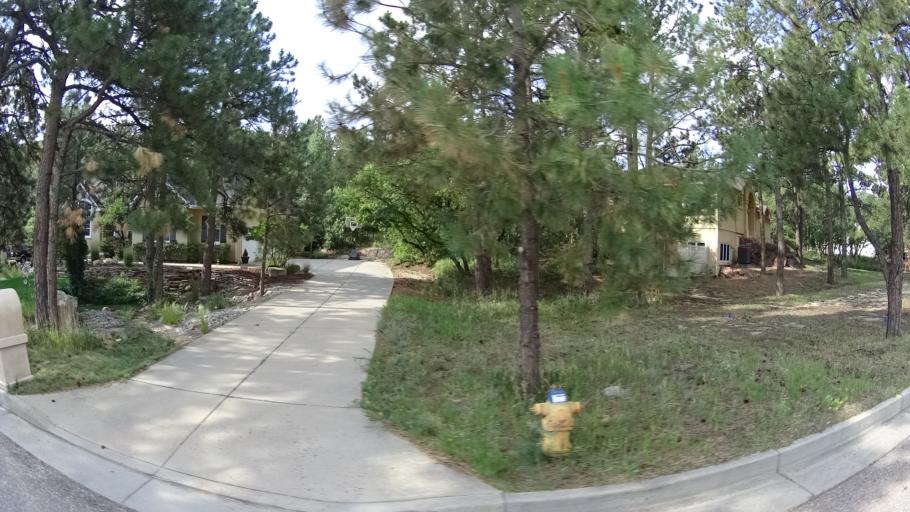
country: US
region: Colorado
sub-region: El Paso County
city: Air Force Academy
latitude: 38.9409
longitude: -104.8278
